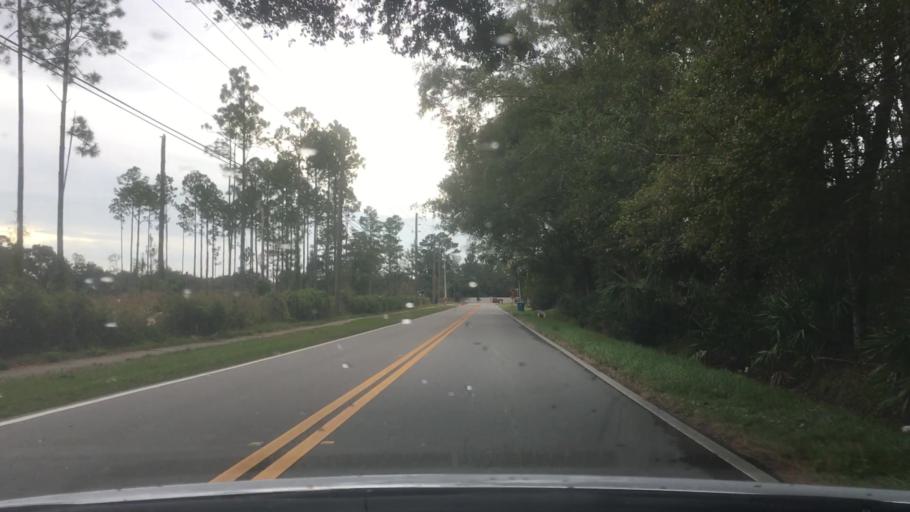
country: US
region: Florida
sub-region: Nassau County
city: Yulee
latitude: 30.5013
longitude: -81.5765
